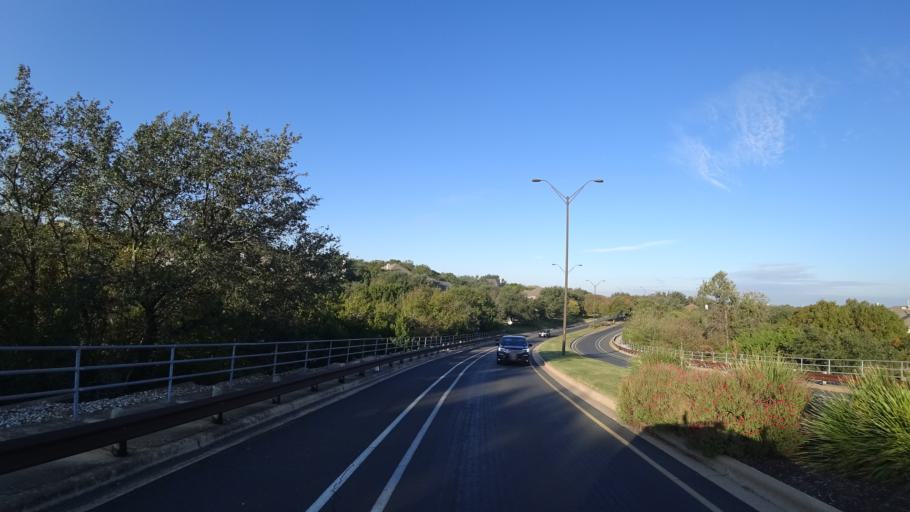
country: US
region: Texas
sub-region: Travis County
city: Hudson Bend
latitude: 30.3762
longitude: -97.8885
